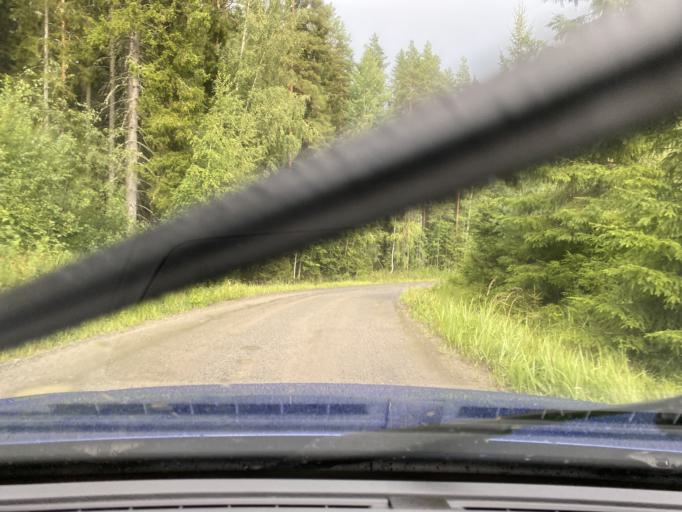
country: FI
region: Pirkanmaa
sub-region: Lounais-Pirkanmaa
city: Punkalaidun
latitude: 61.0624
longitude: 23.2487
